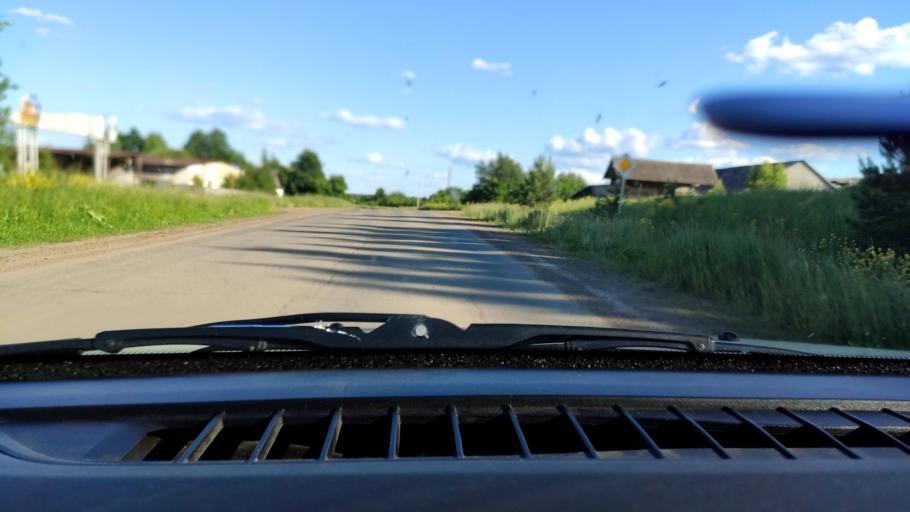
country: RU
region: Perm
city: Uinskoye
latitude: 57.1075
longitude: 56.5324
